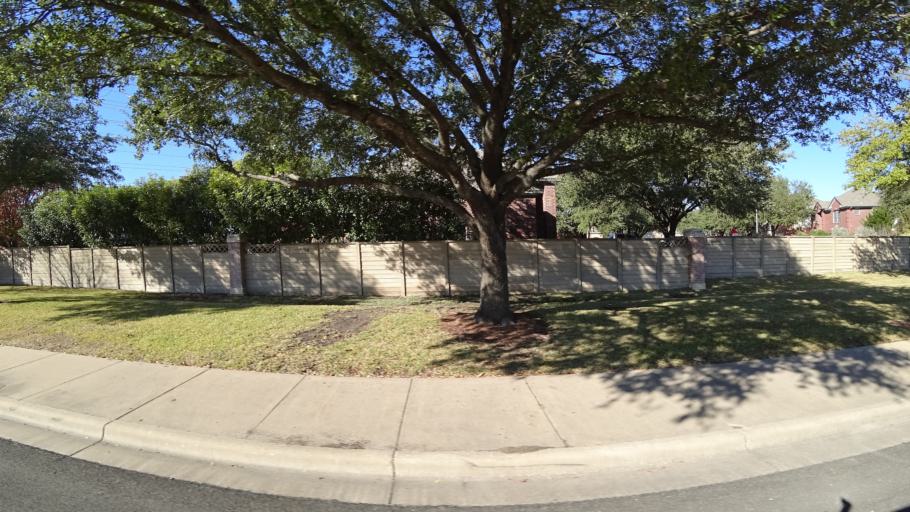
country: US
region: Texas
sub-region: Travis County
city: Wells Branch
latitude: 30.4154
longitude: -97.6879
